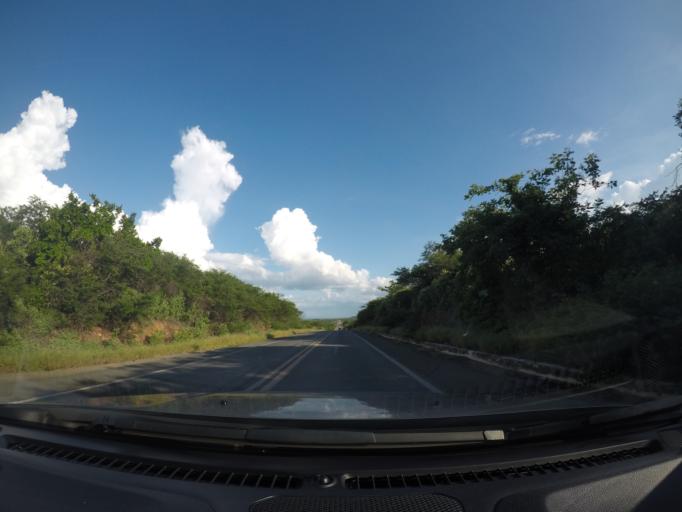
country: BR
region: Bahia
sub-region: Oliveira Dos Brejinhos
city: Oliveira dos Brejinhos
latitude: -12.0705
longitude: -42.9542
